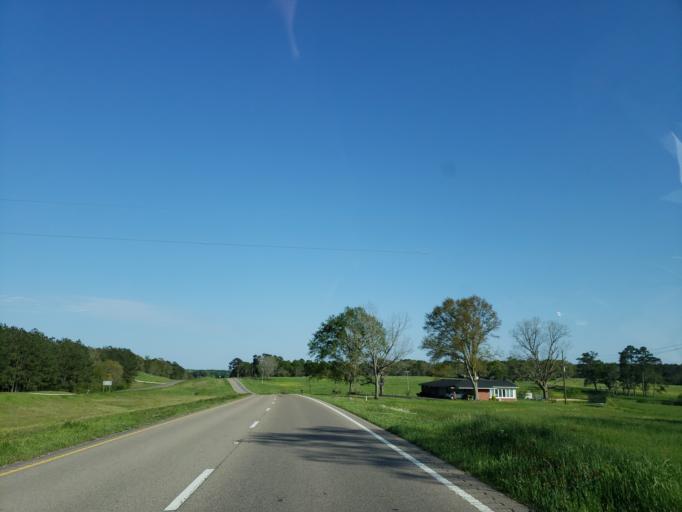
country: US
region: Mississippi
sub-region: Jones County
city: Ellisville
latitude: 31.6890
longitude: -89.3287
